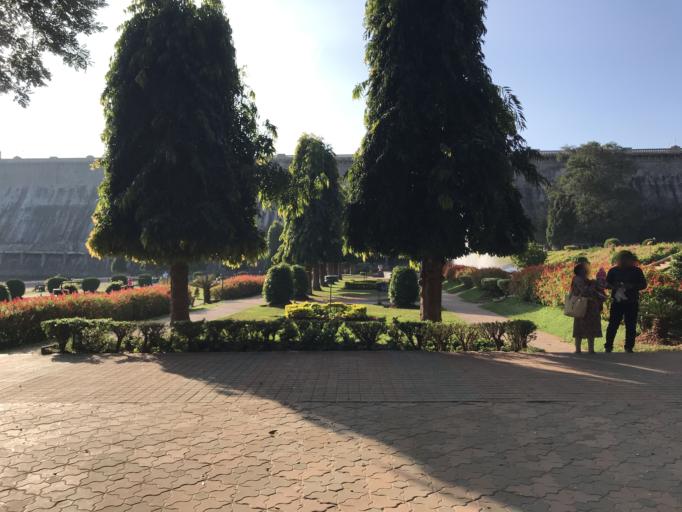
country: IN
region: Karnataka
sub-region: Mandya
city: Shrirangapattana
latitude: 12.4270
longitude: 76.5743
